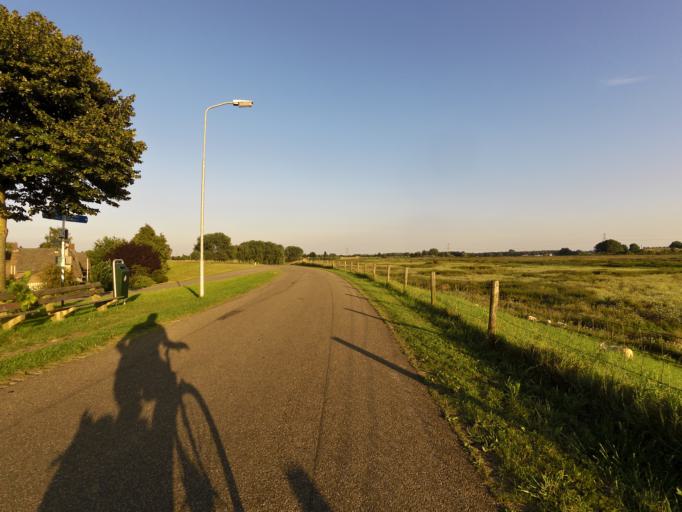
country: NL
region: Gelderland
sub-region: Gemeente Westervoort
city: Westervoort
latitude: 51.9291
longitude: 5.9796
